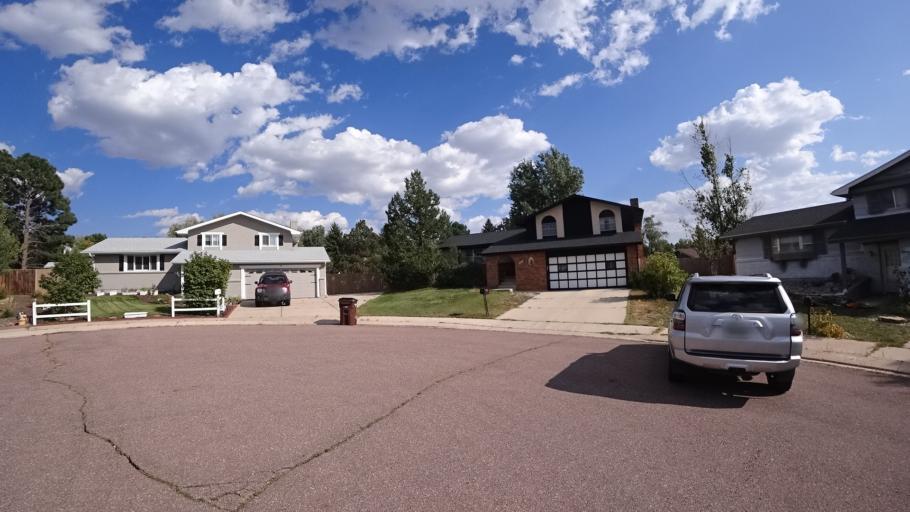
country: US
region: Colorado
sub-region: El Paso County
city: Cimarron Hills
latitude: 38.8740
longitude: -104.7364
